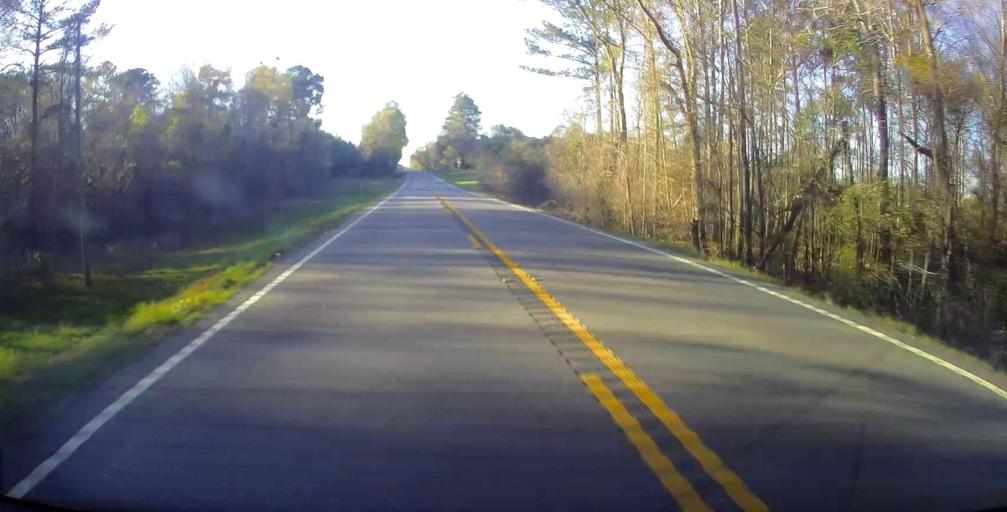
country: US
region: Georgia
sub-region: Pulaski County
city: Hawkinsville
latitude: 32.2379
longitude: -83.4013
